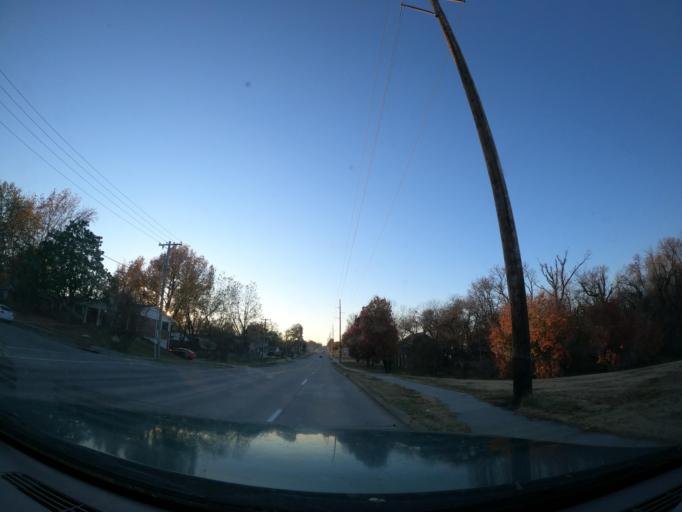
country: US
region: Oklahoma
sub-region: Tulsa County
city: Tulsa
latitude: 36.1408
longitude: -95.8922
